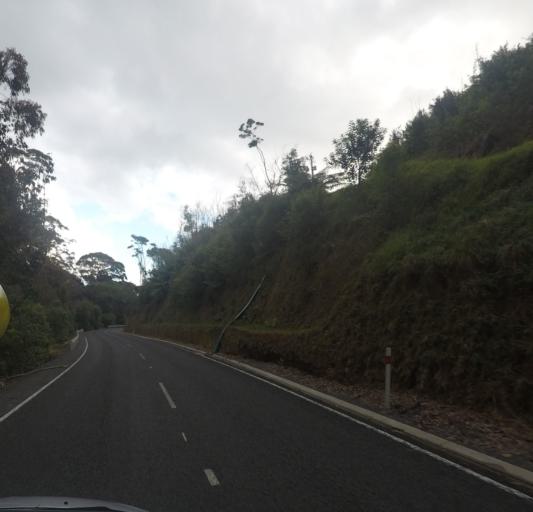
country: NZ
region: Auckland
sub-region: Auckland
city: Warkworth
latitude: -36.3752
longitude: 174.8051
